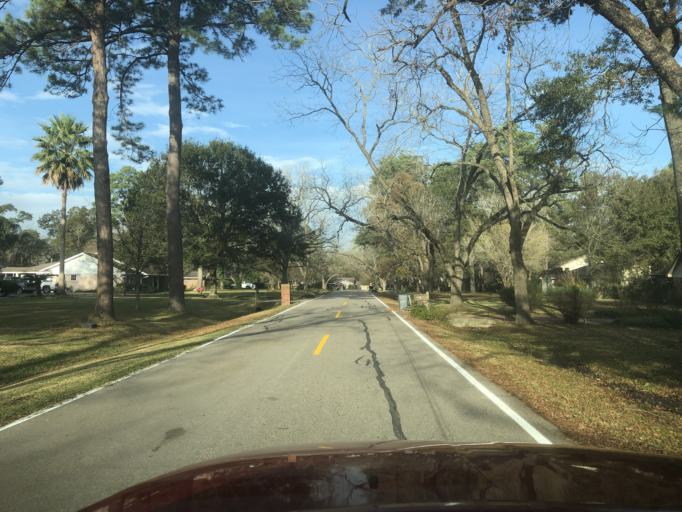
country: US
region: Texas
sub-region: Harris County
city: Spring
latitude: 30.0127
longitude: -95.4731
